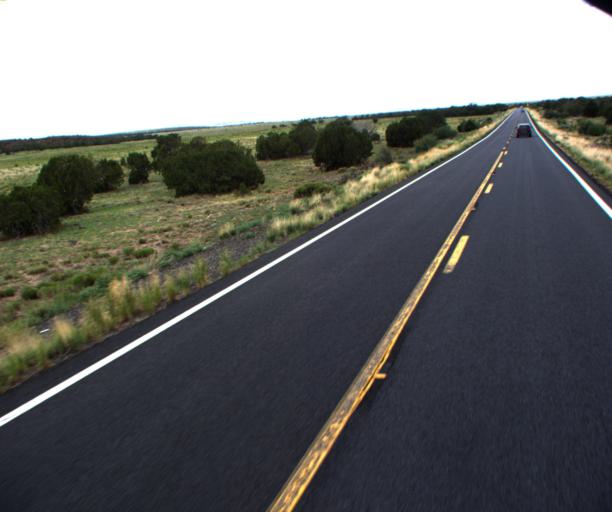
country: US
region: Arizona
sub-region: Coconino County
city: Parks
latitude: 35.5816
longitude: -111.9630
